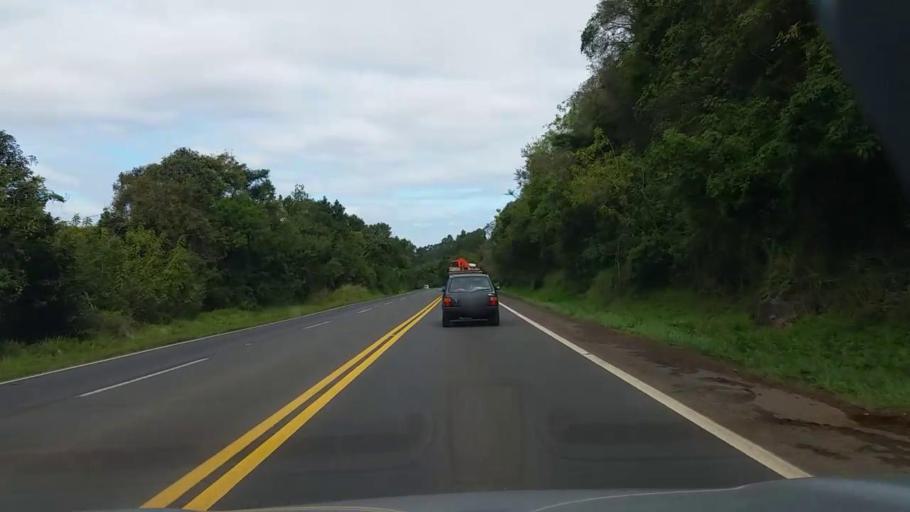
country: BR
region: Rio Grande do Sul
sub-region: Arroio Do Meio
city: Arroio do Meio
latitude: -29.3915
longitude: -52.0421
